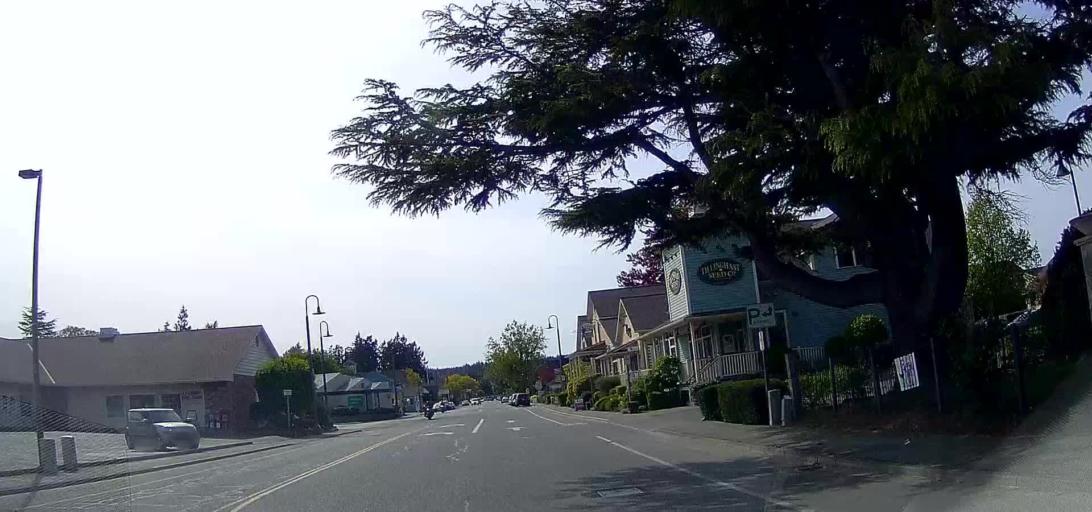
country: US
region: Washington
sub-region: Skagit County
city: Mount Vernon
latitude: 48.3922
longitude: -122.4883
